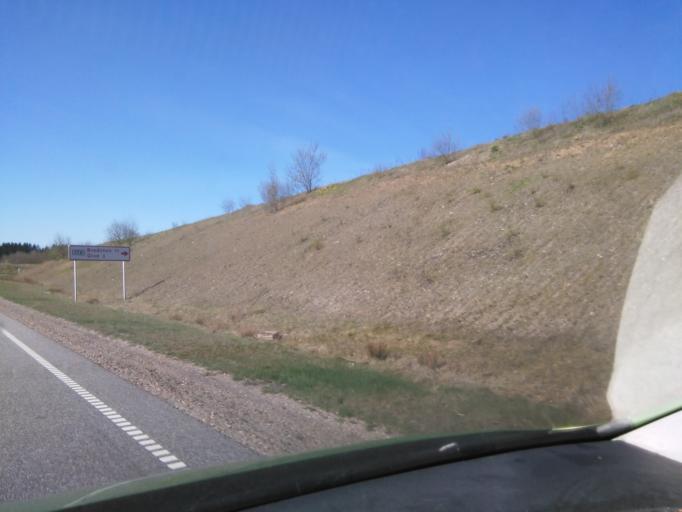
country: DK
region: South Denmark
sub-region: Vejle Kommune
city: Give
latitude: 55.8294
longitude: 9.2575
